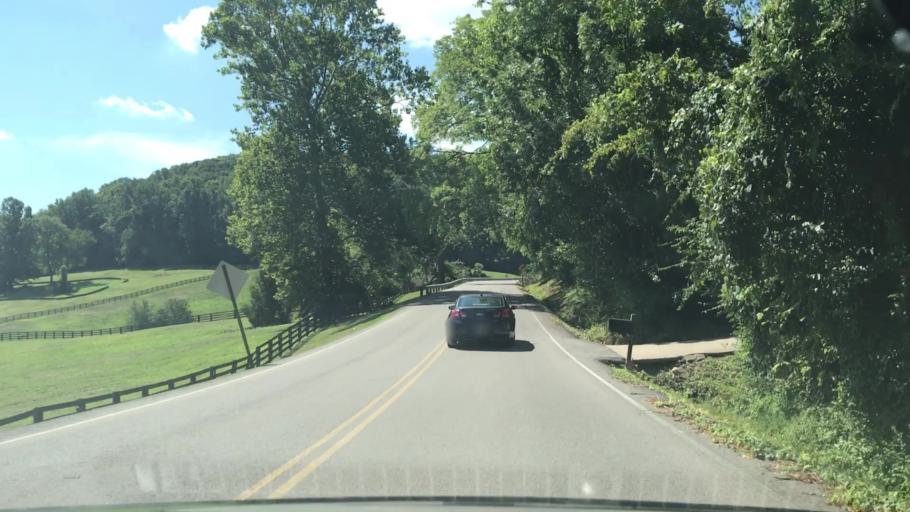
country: US
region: Tennessee
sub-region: Williamson County
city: Franklin
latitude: 35.9711
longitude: -86.8595
